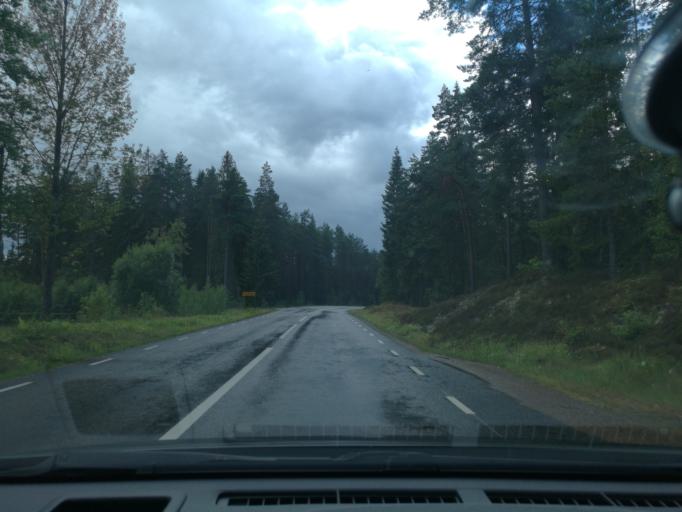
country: SE
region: OEstergoetland
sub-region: Motala Kommun
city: Borensberg
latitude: 58.7460
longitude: 15.3769
